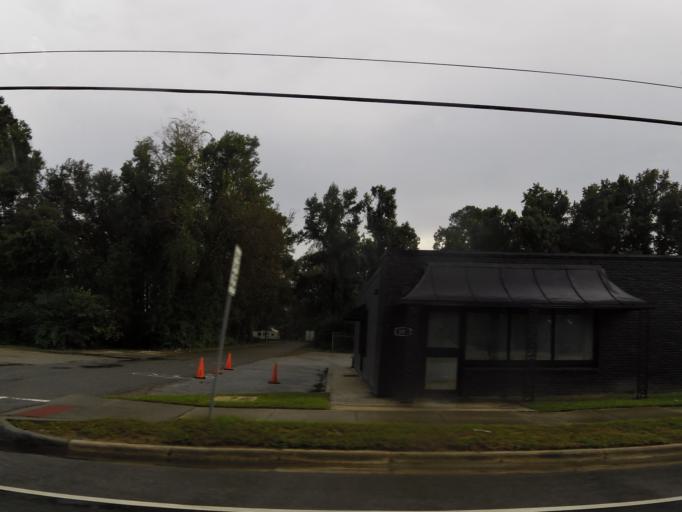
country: US
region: Georgia
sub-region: Long County
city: Ludowici
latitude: 31.7123
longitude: -81.7475
